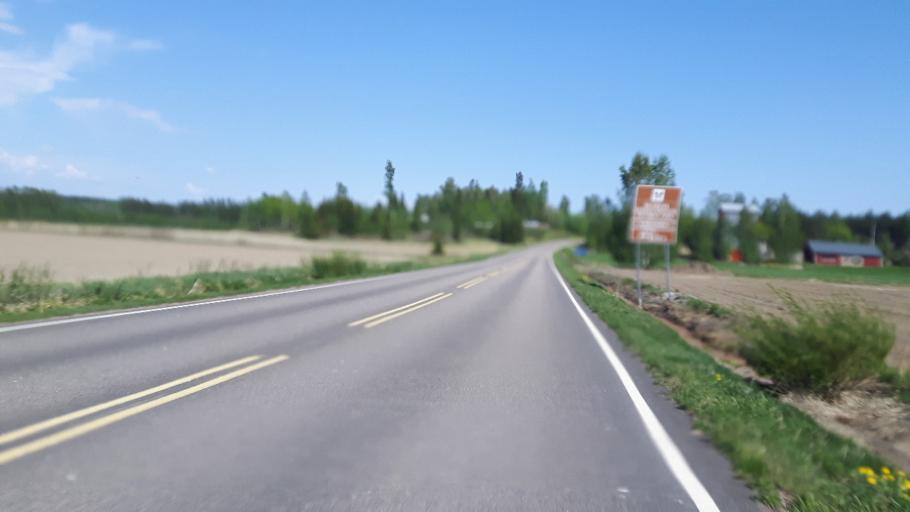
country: FI
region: Kymenlaakso
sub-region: Kotka-Hamina
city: Broby
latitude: 60.4945
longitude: 26.7077
